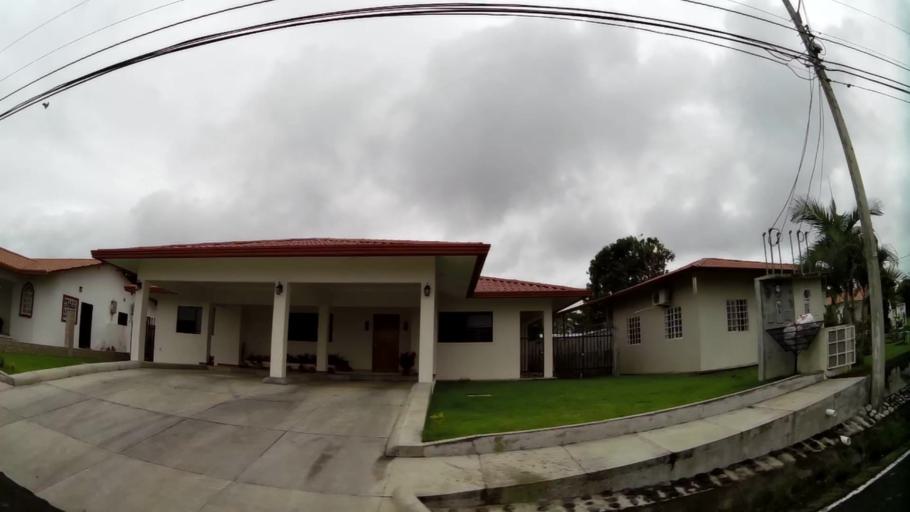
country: PA
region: Chiriqui
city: David
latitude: 8.4366
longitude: -82.4423
